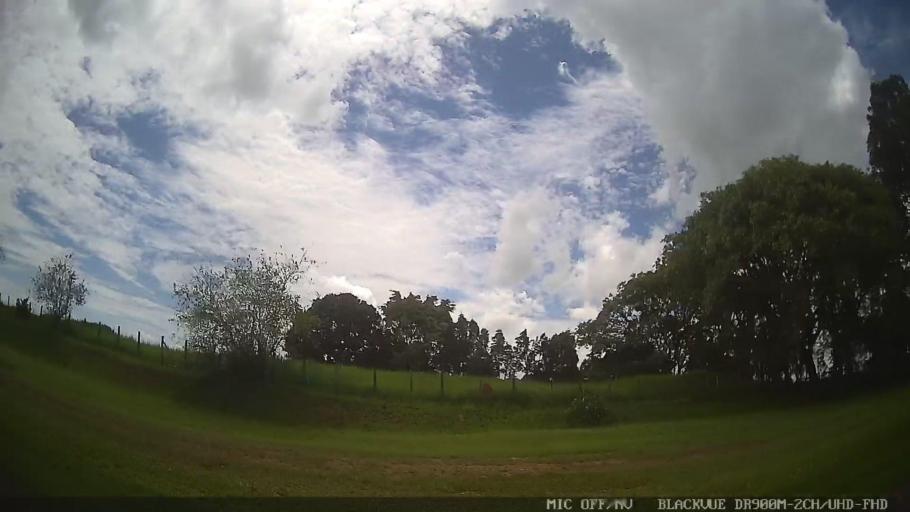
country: BR
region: Sao Paulo
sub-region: Laranjal Paulista
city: Laranjal Paulista
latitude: -23.0446
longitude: -47.9148
